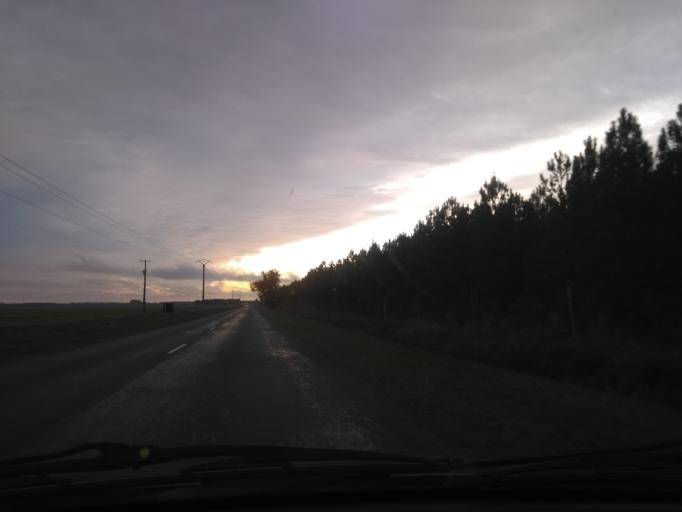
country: FR
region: Aquitaine
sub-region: Departement de la Gironde
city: Saucats
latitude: 44.6259
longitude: -0.6640
